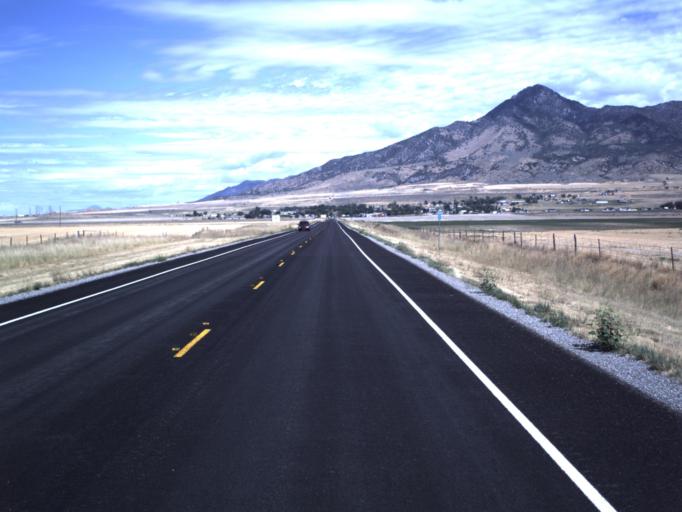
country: US
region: Utah
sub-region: Box Elder County
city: Garland
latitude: 41.8519
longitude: -112.1464
